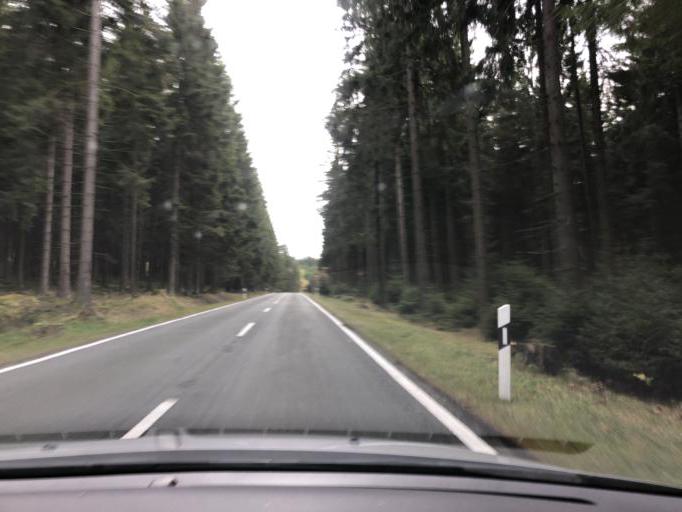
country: DE
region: Thuringia
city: Neuhaus am Rennweg
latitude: 50.5230
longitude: 11.1314
